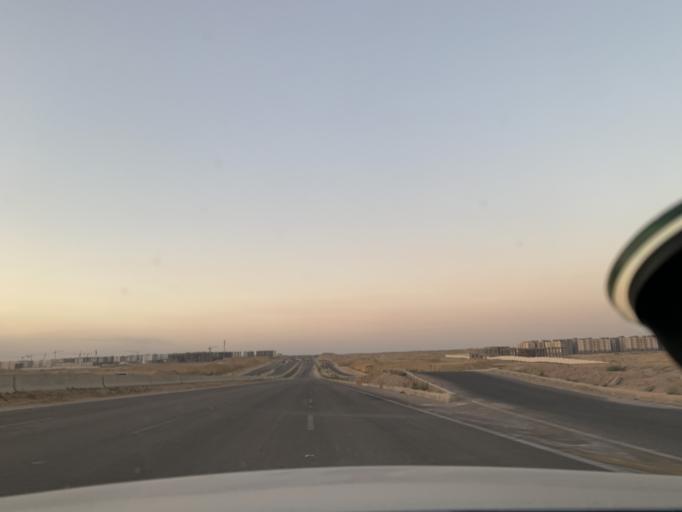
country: EG
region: Muhafazat al Qahirah
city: Halwan
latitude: 29.9559
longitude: 31.5423
